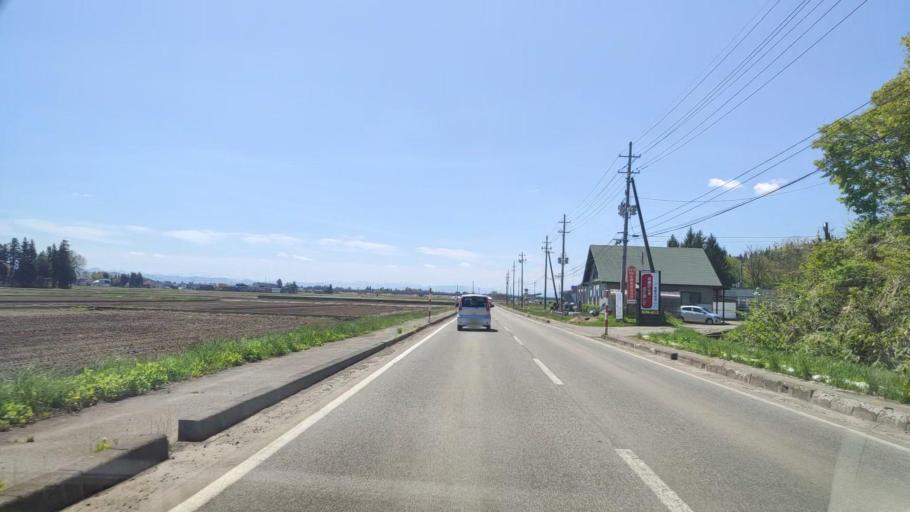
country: JP
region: Akita
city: Omagari
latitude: 39.4441
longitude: 140.4482
